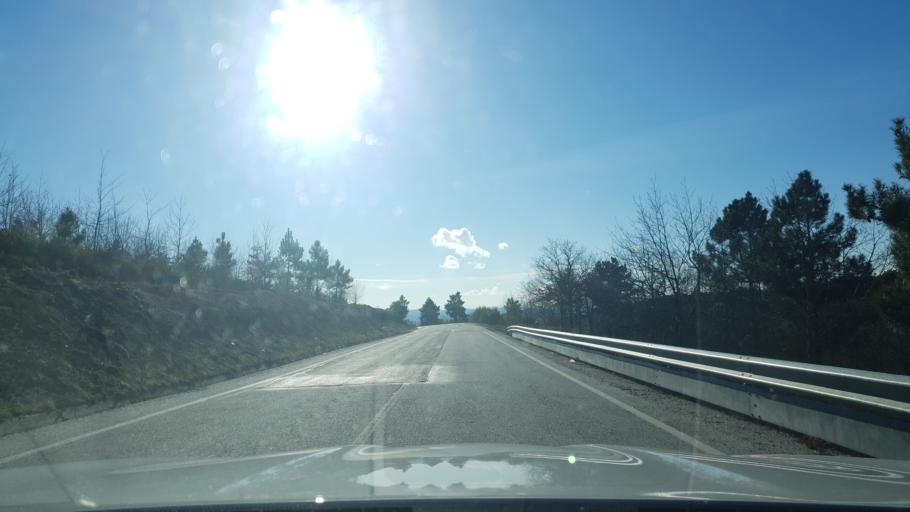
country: PT
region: Braganca
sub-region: Freixo de Espada A Cinta
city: Freixo de Espada a Cinta
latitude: 41.1370
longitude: -6.8064
